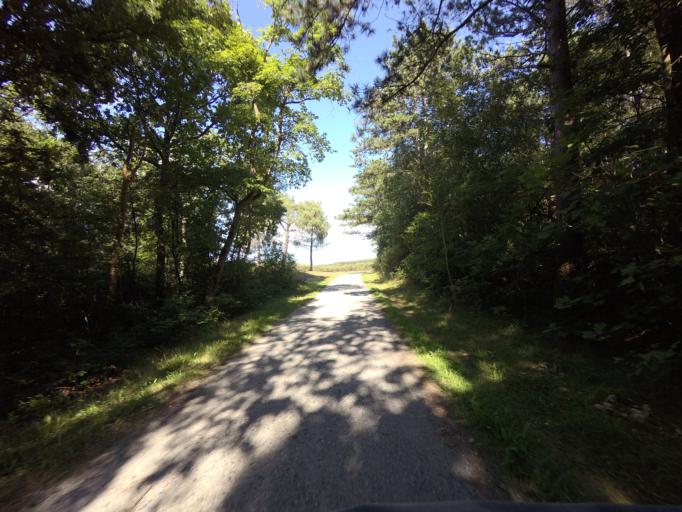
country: NL
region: Friesland
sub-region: Gemeente Terschelling
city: West-Terschelling
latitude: 53.3758
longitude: 5.2315
